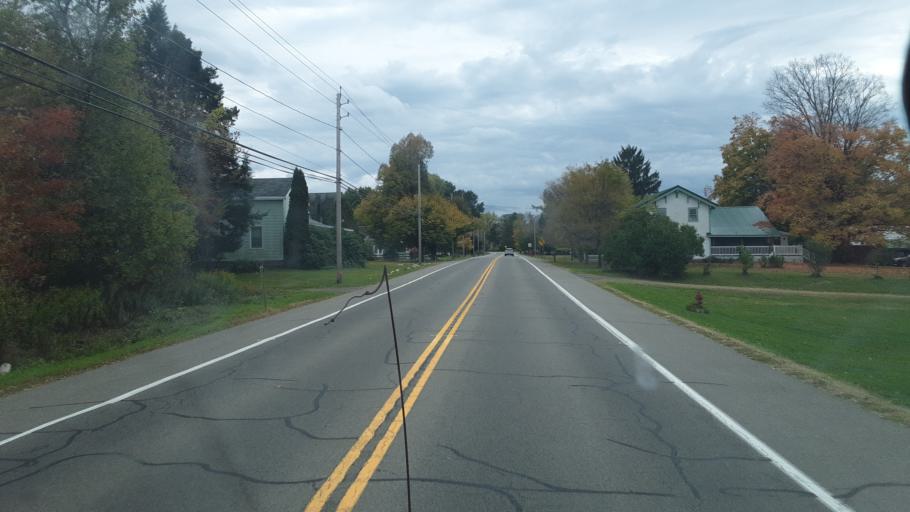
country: US
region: New York
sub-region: Allegany County
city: Belmont
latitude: 42.2172
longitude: -78.0221
